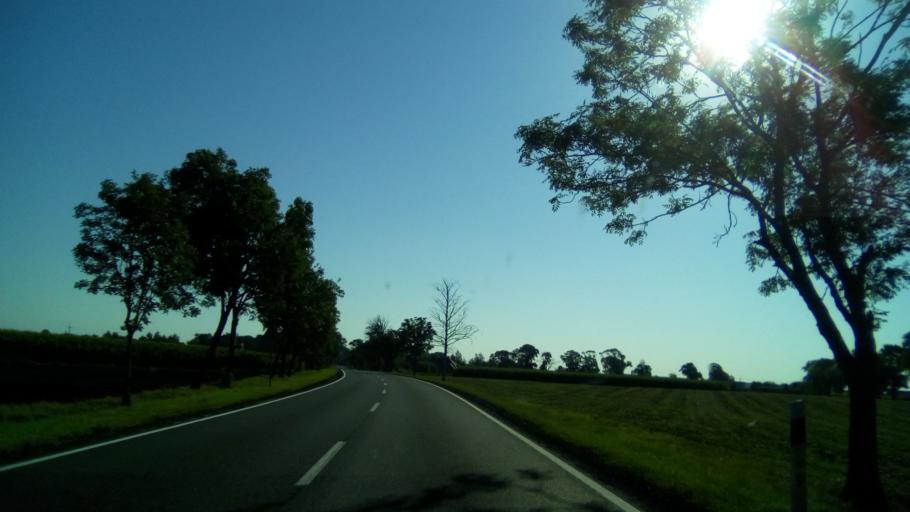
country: PL
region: Kujawsko-Pomorskie
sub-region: Powiat radziejowski
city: Radziejow
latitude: 52.6174
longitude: 18.4834
